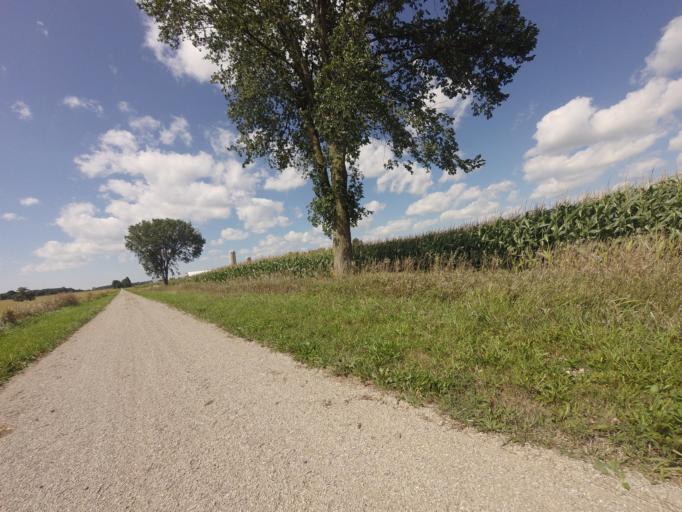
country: CA
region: Ontario
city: Huron East
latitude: 43.6639
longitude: -81.2598
